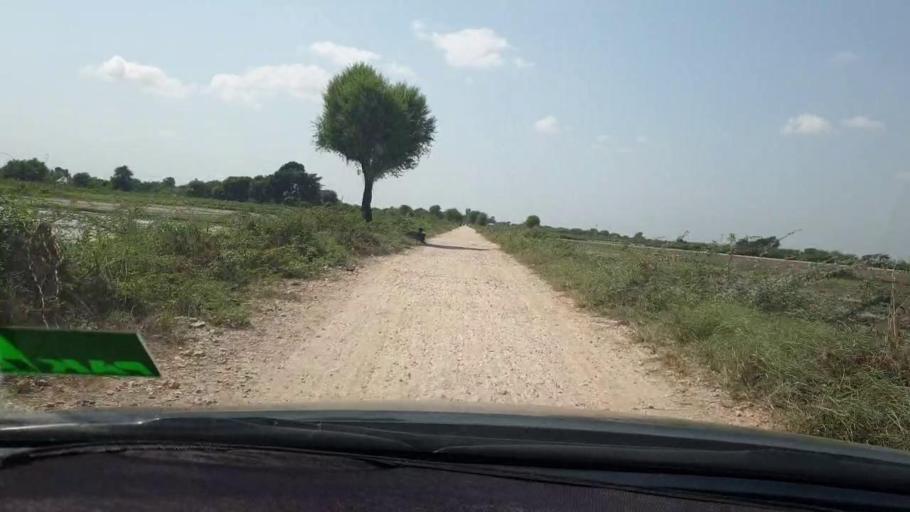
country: PK
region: Sindh
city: Naukot
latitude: 24.9149
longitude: 69.2672
